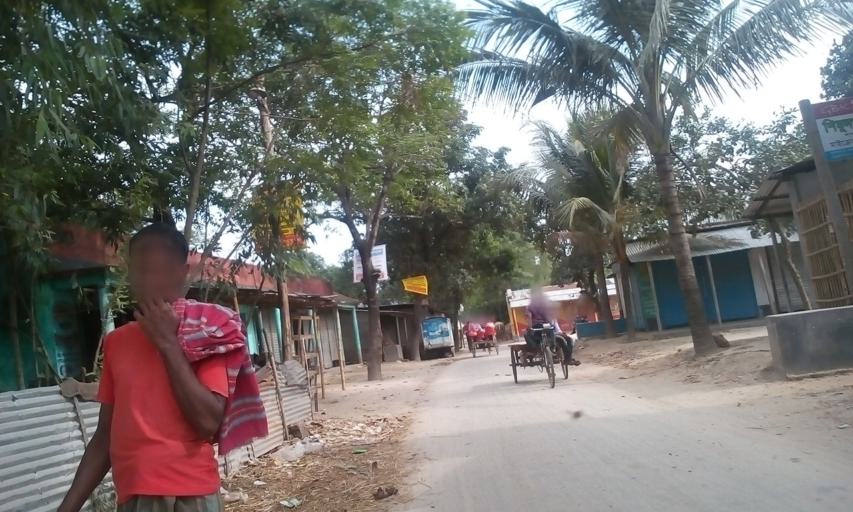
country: IN
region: West Bengal
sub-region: Dakshin Dinajpur
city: Balurghat
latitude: 25.3820
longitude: 88.9834
